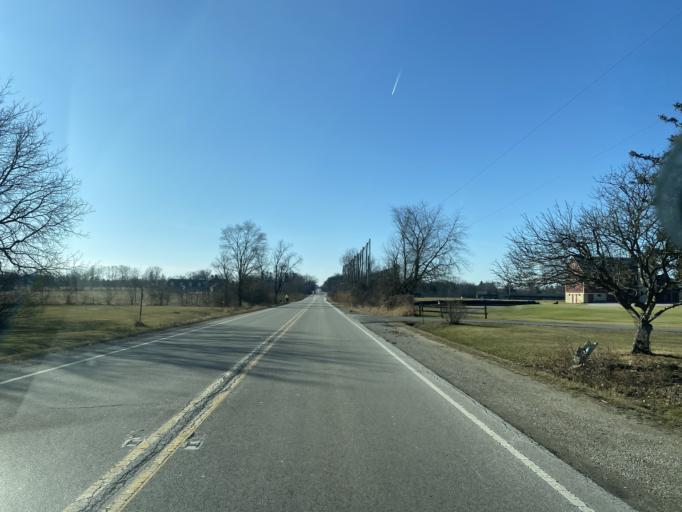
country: US
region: Illinois
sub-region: Will County
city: Goodings Grove
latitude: 41.6759
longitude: -87.9466
